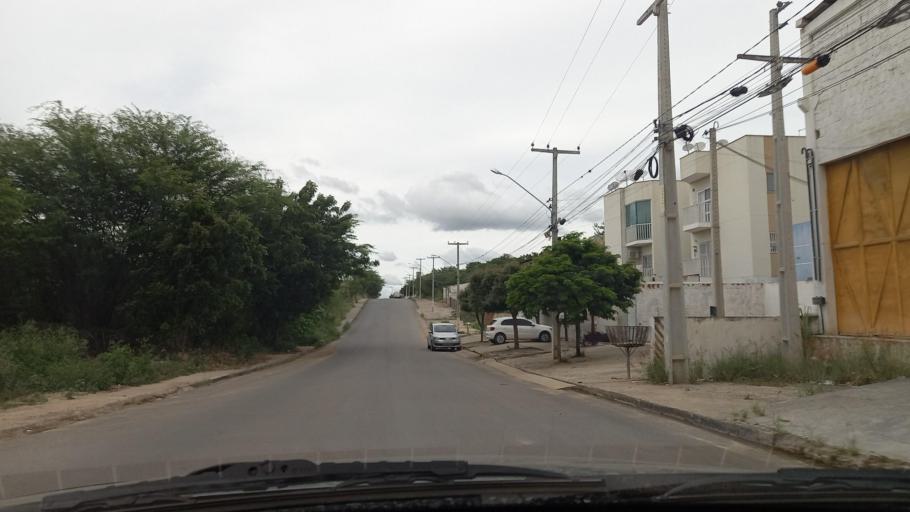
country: BR
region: Pernambuco
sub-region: Gravata
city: Gravata
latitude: -8.2127
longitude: -35.6020
